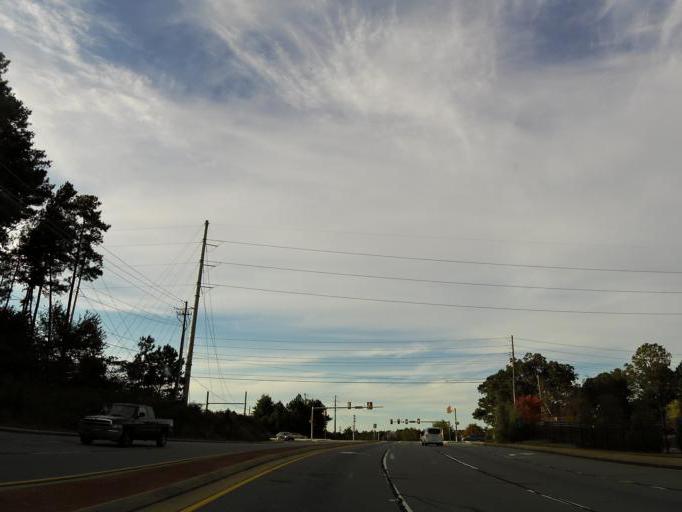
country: US
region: Georgia
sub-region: Cobb County
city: Kennesaw
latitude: 34.0484
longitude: -84.5840
